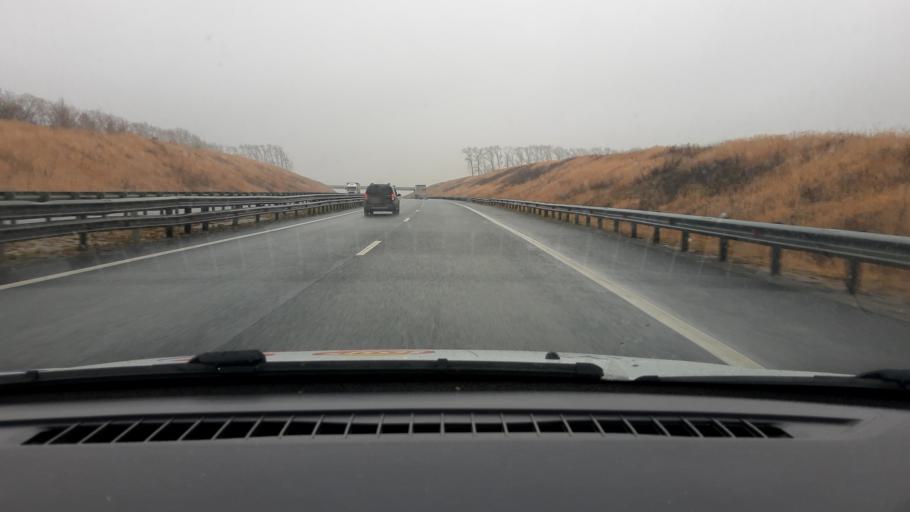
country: RU
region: Nizjnij Novgorod
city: Burevestnik
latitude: 56.1572
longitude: 43.7482
